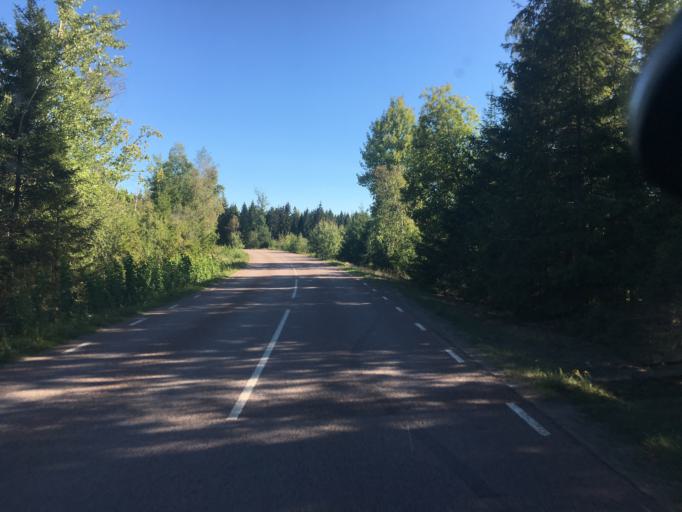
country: SE
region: Vaestmanland
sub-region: Vasteras
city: Tillberga
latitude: 59.7253
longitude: 16.6718
